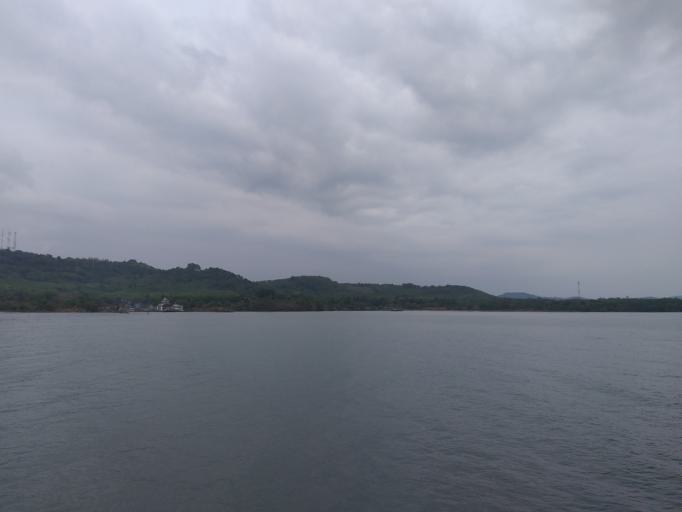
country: TH
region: Trat
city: Laem Ngop
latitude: 12.1797
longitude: 102.3011
